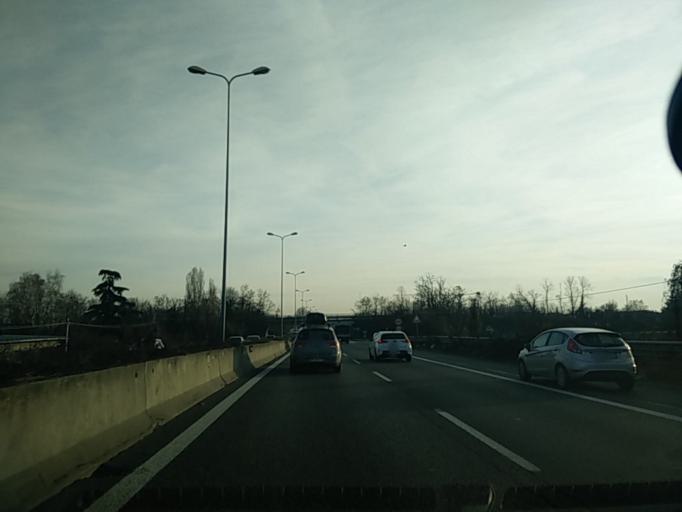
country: IT
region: Lombardy
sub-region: Provincia di Monza e Brianza
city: Varedo
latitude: 45.5867
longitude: 9.1743
